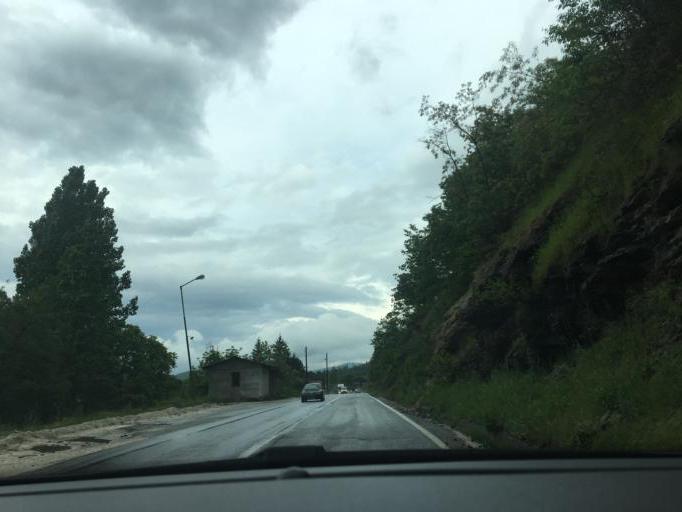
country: MK
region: Debarca
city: Belcista
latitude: 41.2833
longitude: 20.7893
